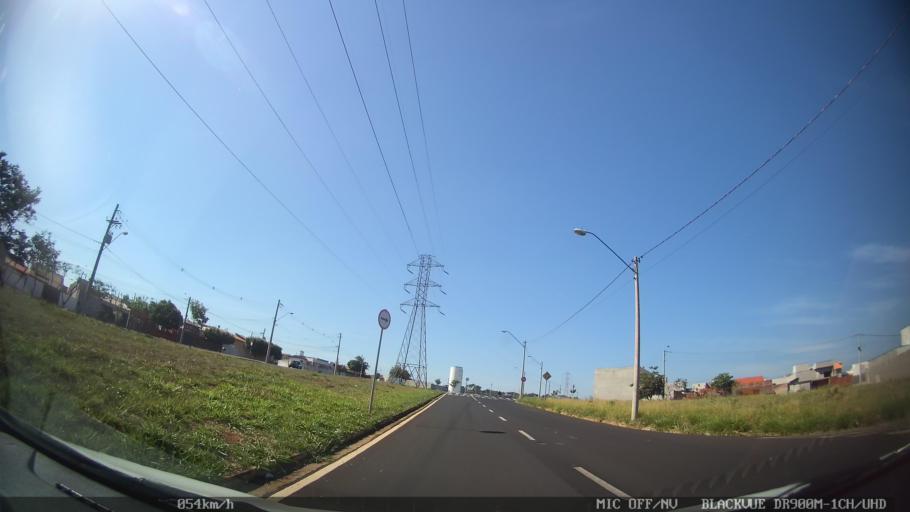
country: BR
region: Sao Paulo
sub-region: Sao Jose Do Rio Preto
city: Sao Jose do Rio Preto
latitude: -20.7657
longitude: -49.3581
